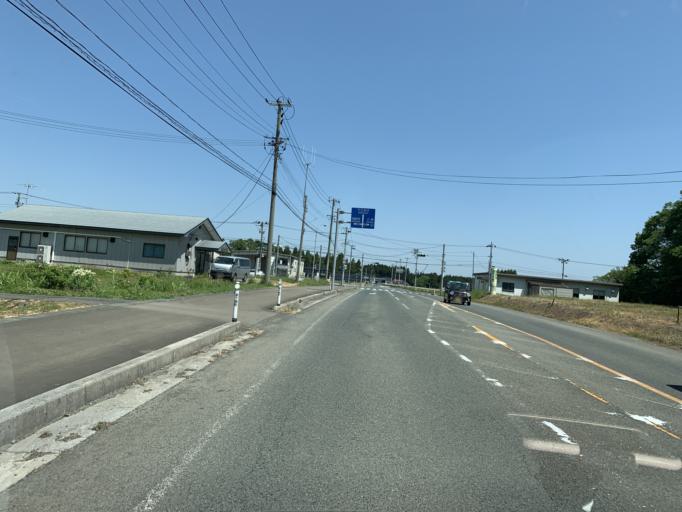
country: JP
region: Iwate
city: Kitakami
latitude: 39.2320
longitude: 141.0667
